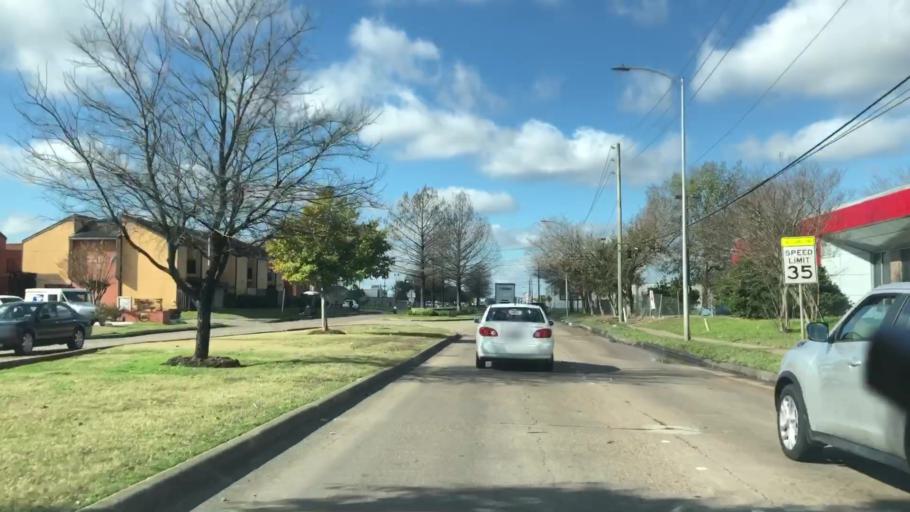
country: US
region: Texas
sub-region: Fort Bend County
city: Missouri City
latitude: 29.6561
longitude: -95.5038
